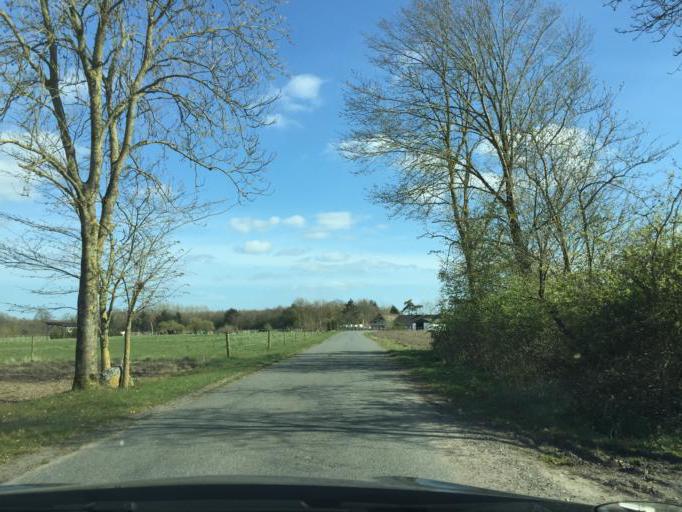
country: DK
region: South Denmark
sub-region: Kerteminde Kommune
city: Langeskov
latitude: 55.3049
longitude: 10.5621
